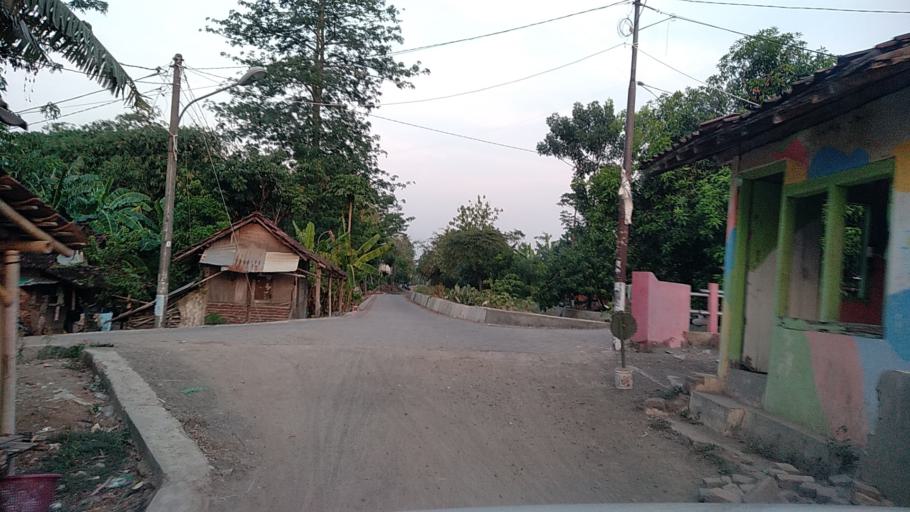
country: ID
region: Central Java
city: Semarang
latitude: -6.9712
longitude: 110.3084
